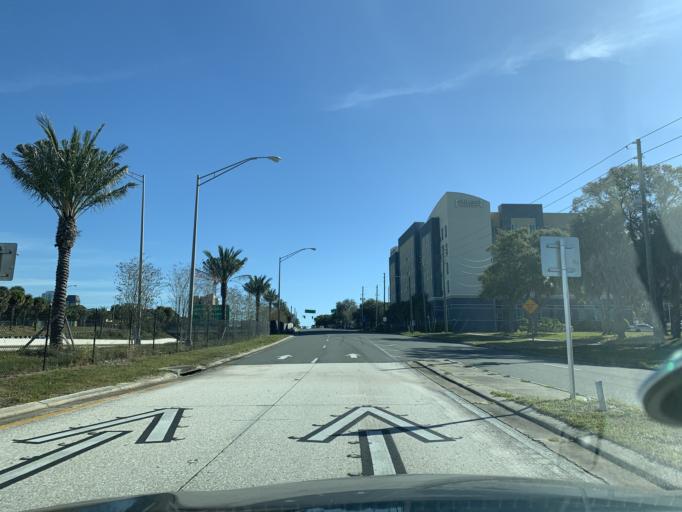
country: US
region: Florida
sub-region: Pinellas County
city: Saint Petersburg
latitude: 27.7657
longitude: -82.6490
